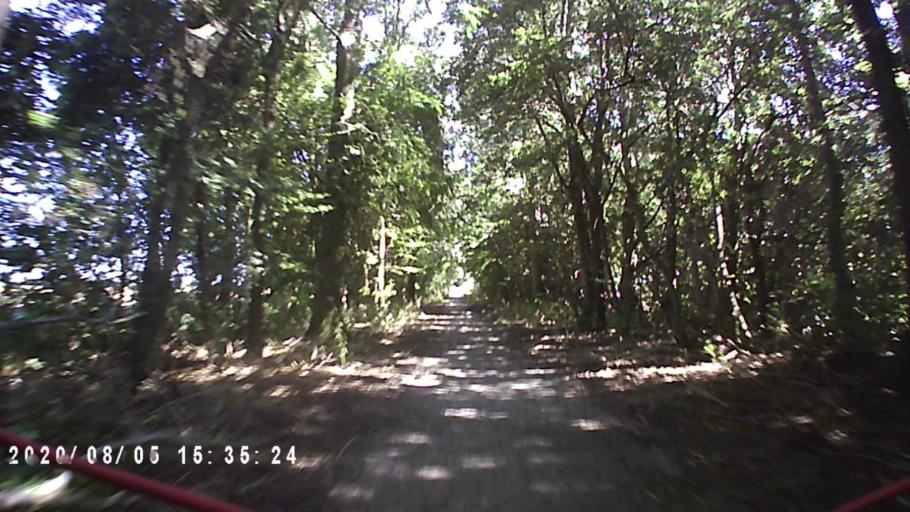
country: NL
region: Groningen
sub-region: Gemeente Winsum
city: Winsum
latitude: 53.3632
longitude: 6.4657
